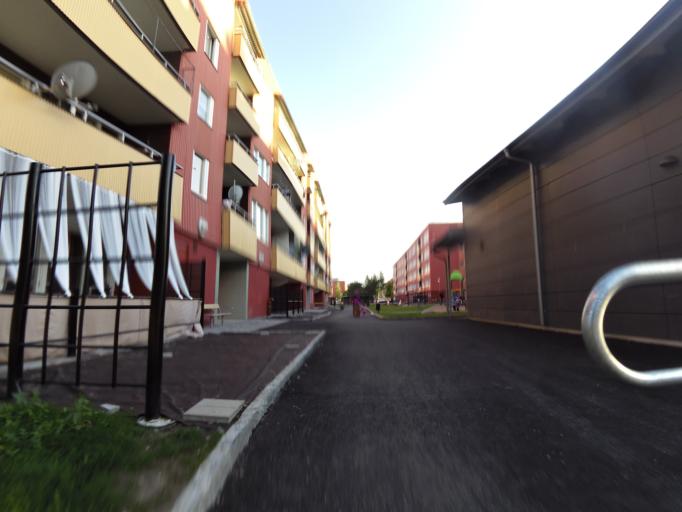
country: SE
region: Gaevleborg
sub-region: Gavle Kommun
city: Gavle
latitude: 60.6531
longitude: 17.1354
